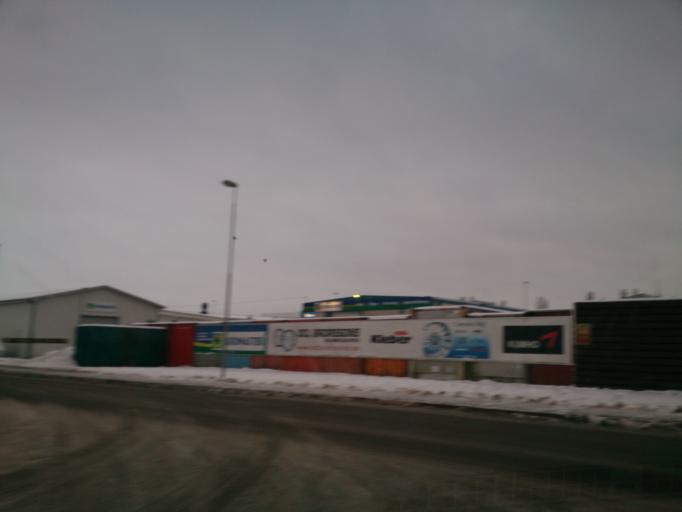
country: SE
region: OEstergoetland
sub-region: Linkopings Kommun
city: Linkoping
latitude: 58.4166
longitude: 15.6399
